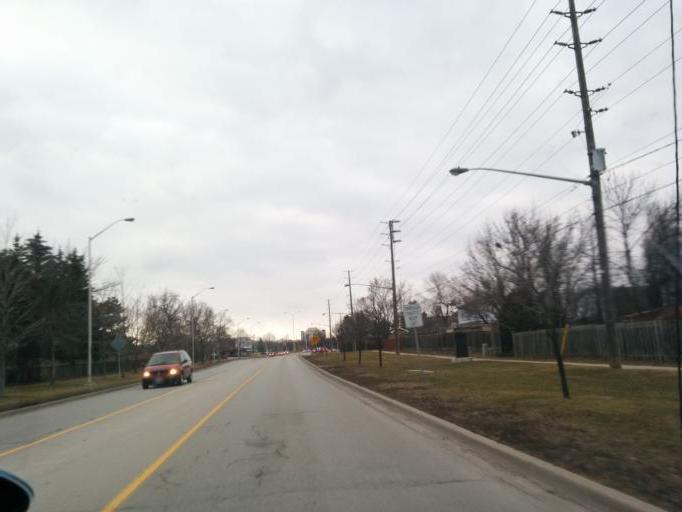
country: CA
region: Ontario
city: Oakville
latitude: 43.4012
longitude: -79.7285
